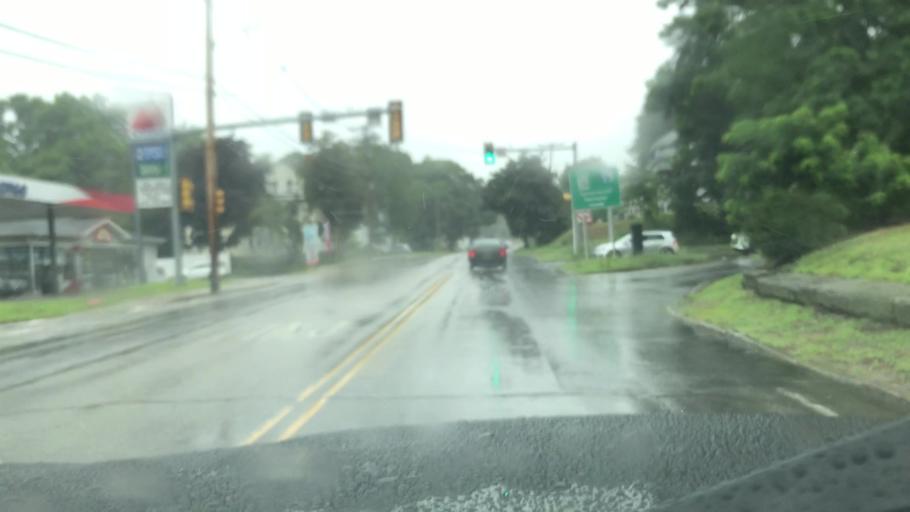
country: US
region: New Hampshire
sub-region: Strafford County
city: Dover
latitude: 43.1822
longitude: -70.8759
